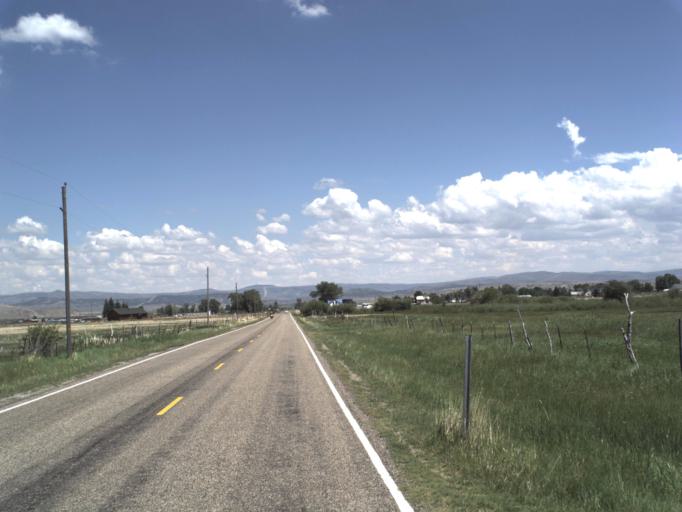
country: US
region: Utah
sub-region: Rich County
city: Randolph
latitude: 41.5241
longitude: -111.1786
